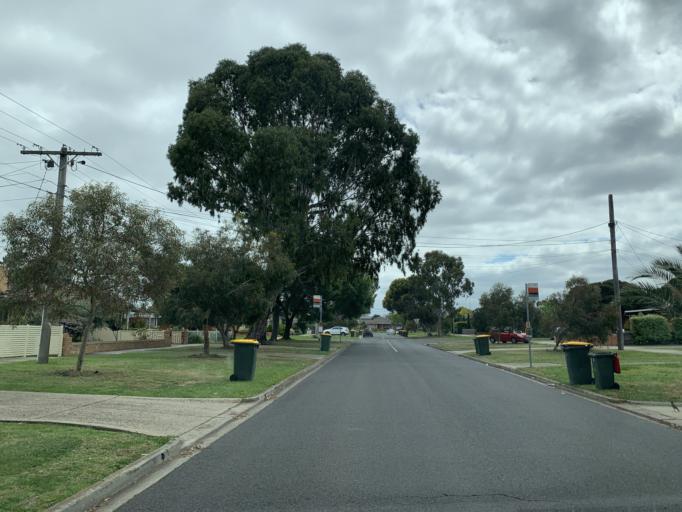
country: AU
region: Victoria
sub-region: Maribyrnong
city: Braybrook
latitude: -37.7672
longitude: 144.8576
